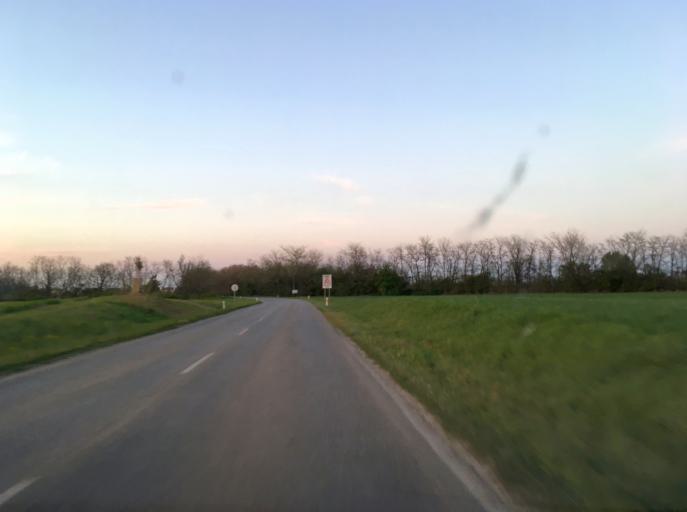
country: SK
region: Nitriansky
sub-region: Okres Nove Zamky
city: Nove Zamky
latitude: 47.9500
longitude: 18.1380
